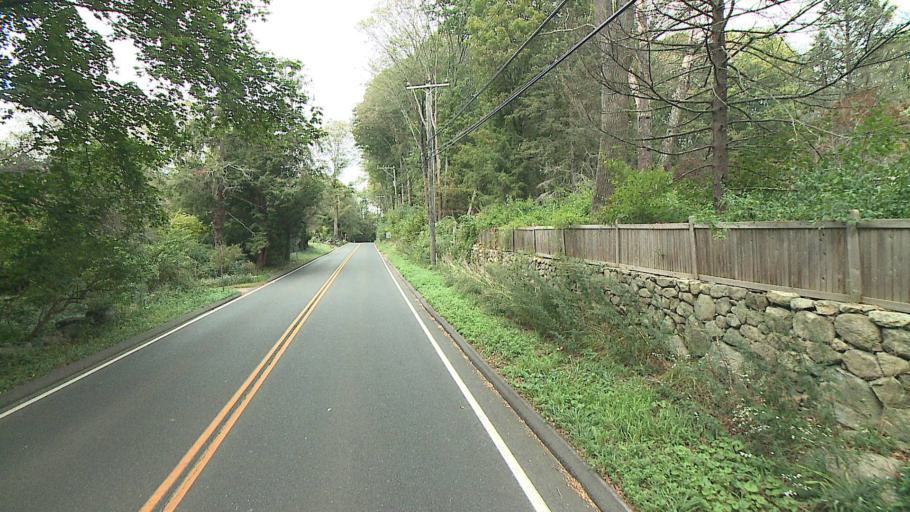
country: US
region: Connecticut
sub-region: Fairfield County
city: Ridgefield
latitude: 41.2337
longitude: -73.4824
